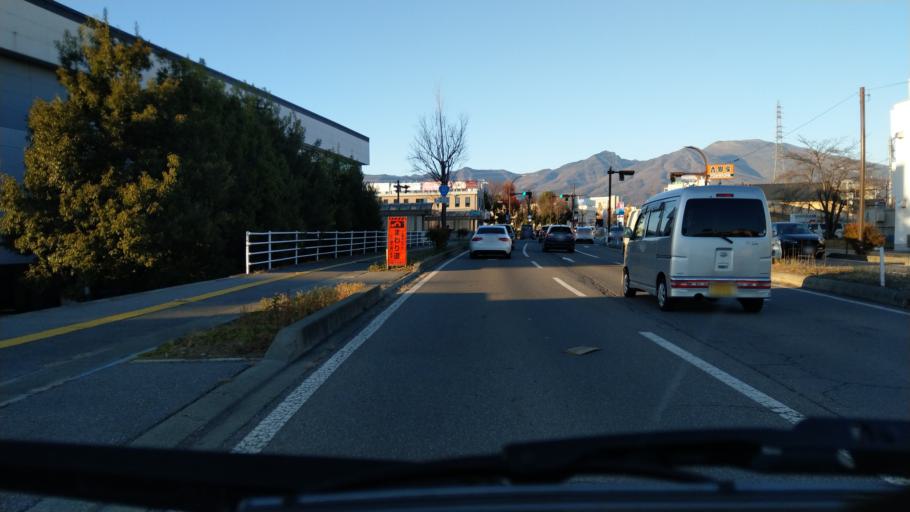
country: JP
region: Nagano
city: Komoro
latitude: 36.2732
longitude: 138.4655
